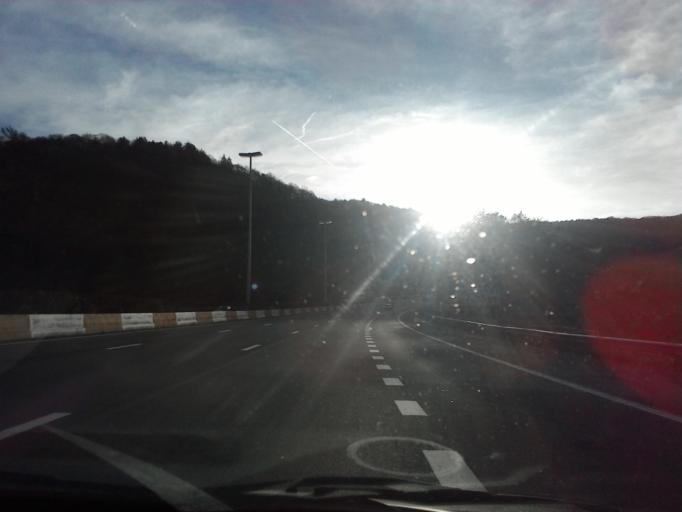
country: BE
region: Wallonia
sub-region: Province de Liege
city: Chaudfontaine
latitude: 50.5787
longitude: 5.6044
